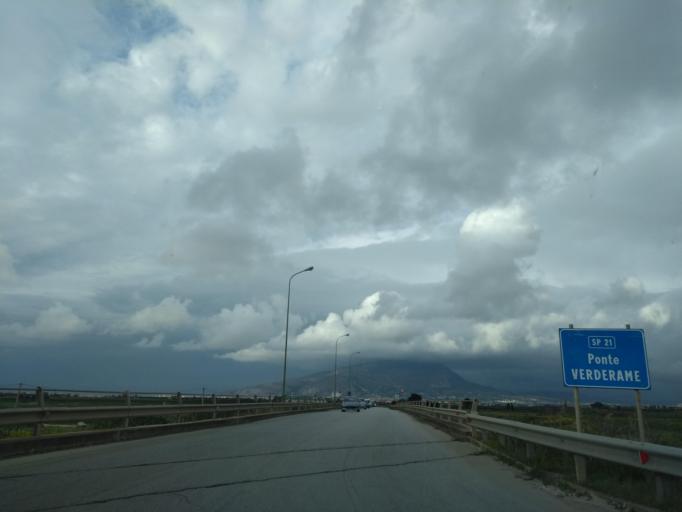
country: IT
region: Sicily
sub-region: Trapani
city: Marausa
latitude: 37.9686
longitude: 12.5216
